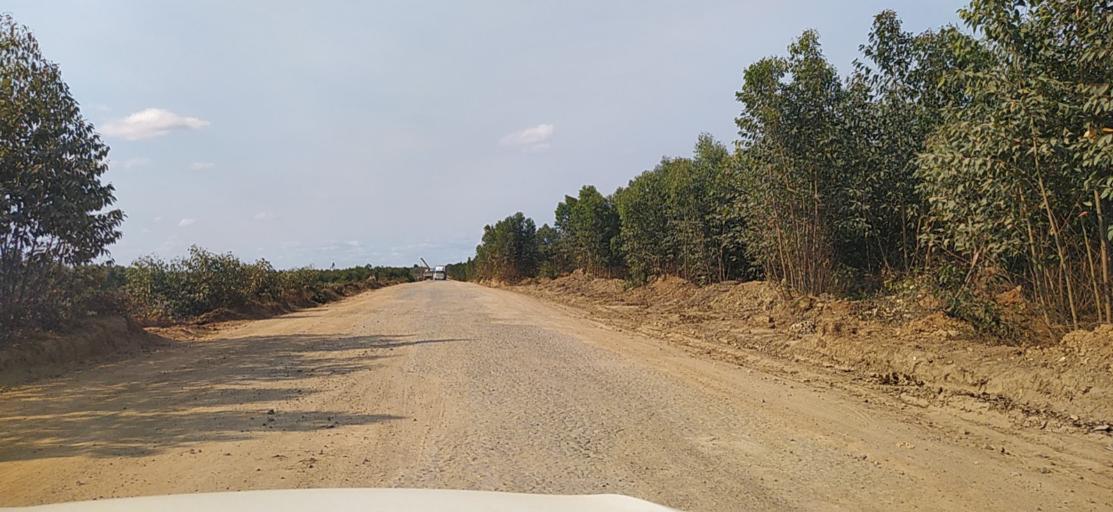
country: MG
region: Alaotra Mangoro
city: Moramanga
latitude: -18.6868
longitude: 48.2712
